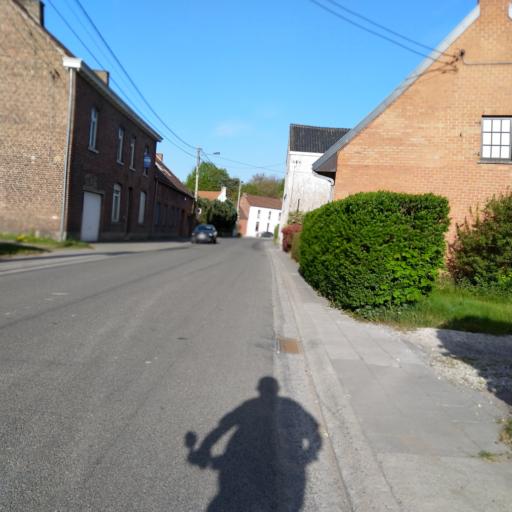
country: BE
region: Wallonia
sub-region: Province du Hainaut
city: Jurbise
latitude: 50.5066
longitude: 3.8848
